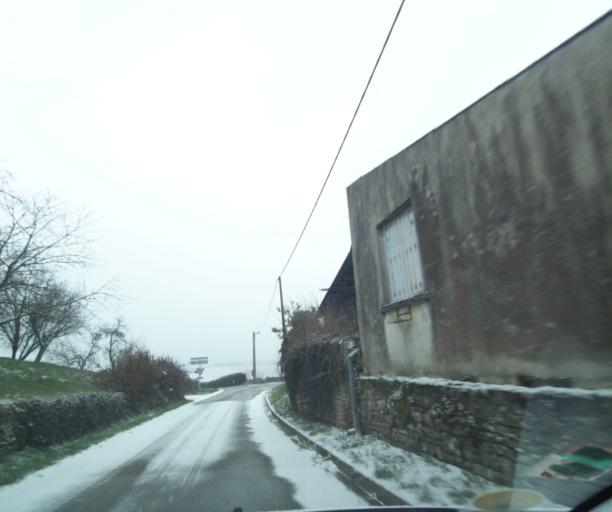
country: FR
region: Champagne-Ardenne
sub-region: Departement de la Haute-Marne
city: Wassy
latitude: 48.4751
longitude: 5.0360
